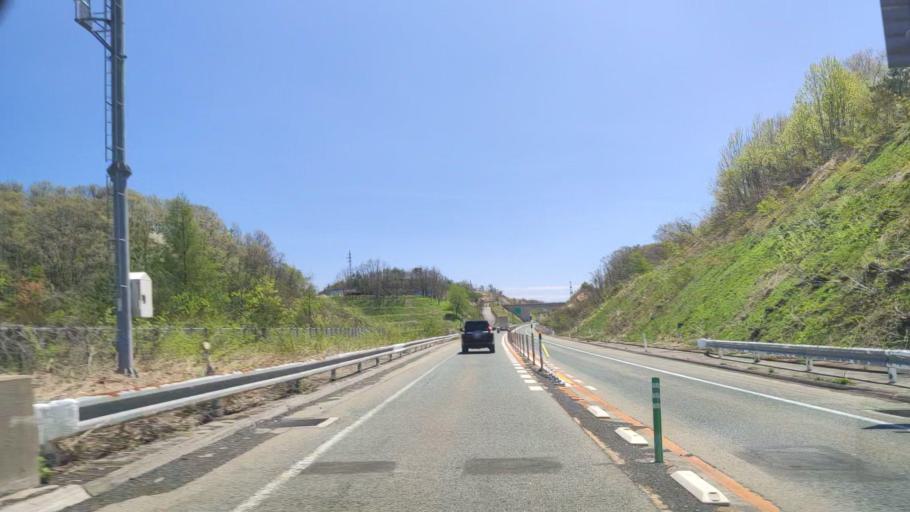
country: JP
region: Yamagata
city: Shinjo
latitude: 38.7259
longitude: 140.3073
